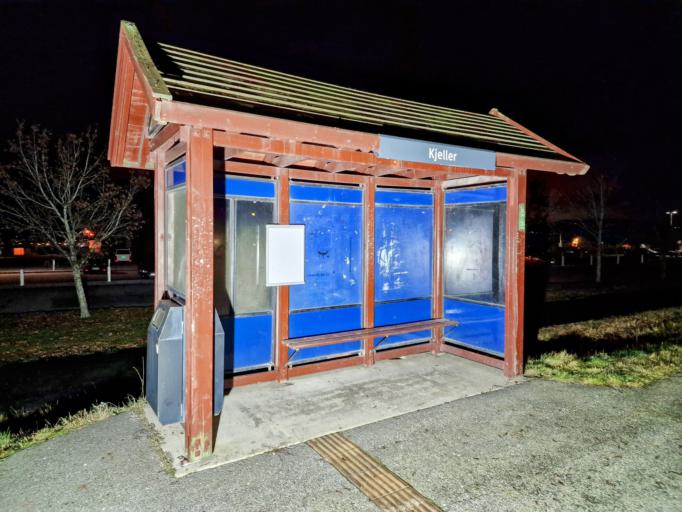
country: NO
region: Akershus
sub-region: Skedsmo
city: Lillestrom
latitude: 59.9715
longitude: 11.0457
